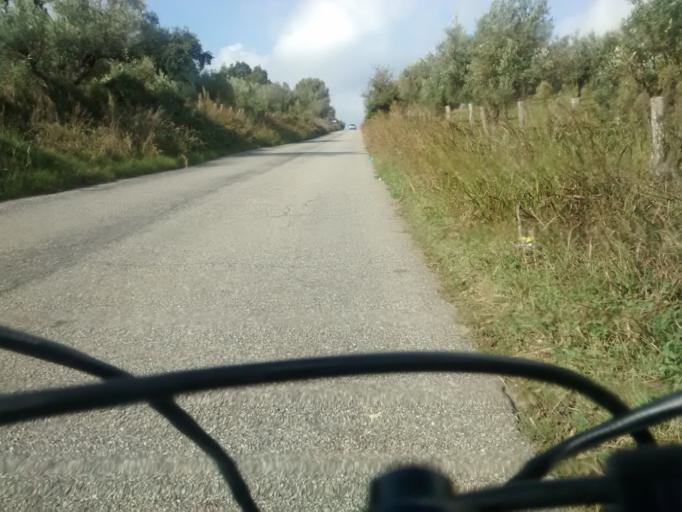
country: IT
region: Calabria
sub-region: Provincia di Catanzaro
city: Cortale
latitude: 38.8800
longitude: 16.4126
